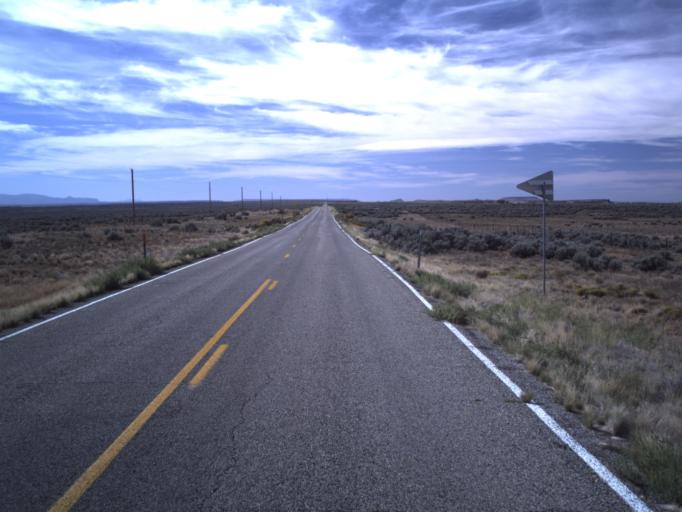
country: US
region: Utah
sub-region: San Juan County
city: Blanding
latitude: 37.4158
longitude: -109.3345
